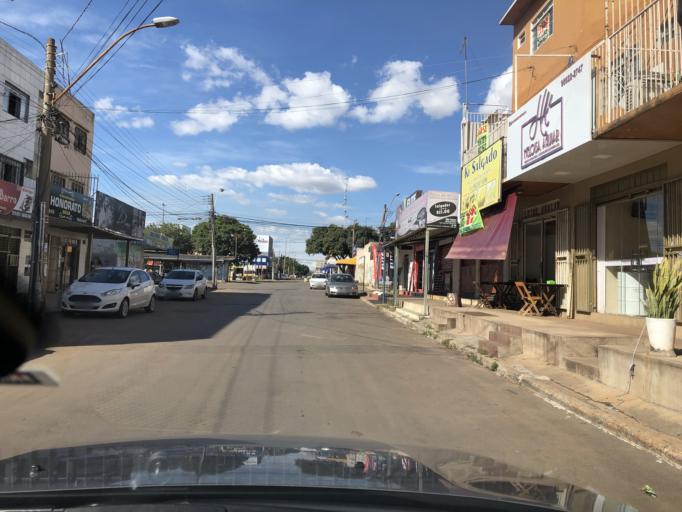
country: BR
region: Federal District
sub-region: Brasilia
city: Brasilia
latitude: -15.7919
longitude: -48.1235
